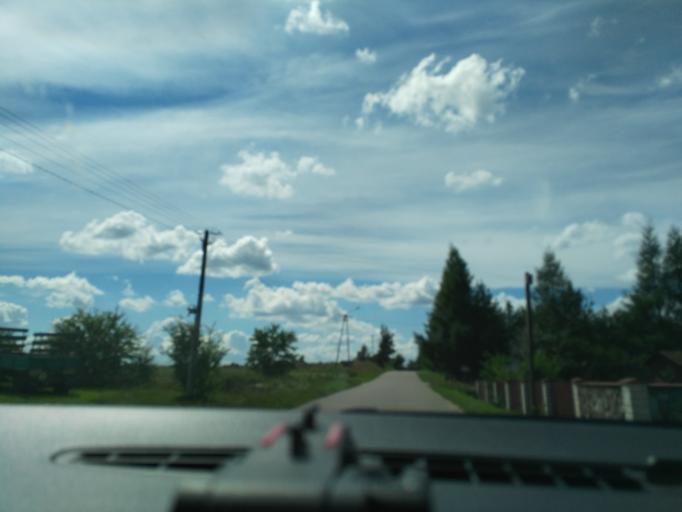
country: PL
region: Podlasie
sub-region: Powiat sejnenski
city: Sejny
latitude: 54.0319
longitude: 23.3388
